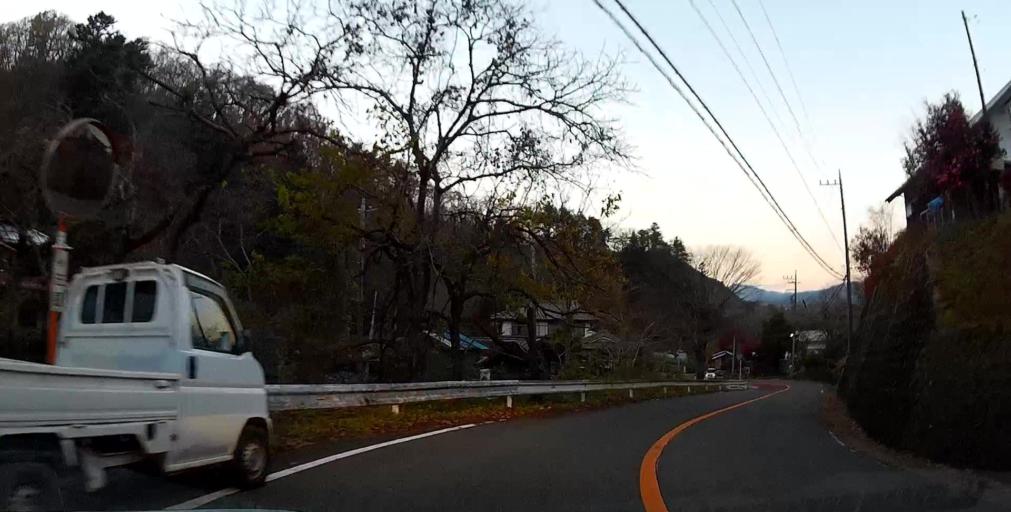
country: JP
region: Yamanashi
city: Uenohara
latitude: 35.5858
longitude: 139.1732
